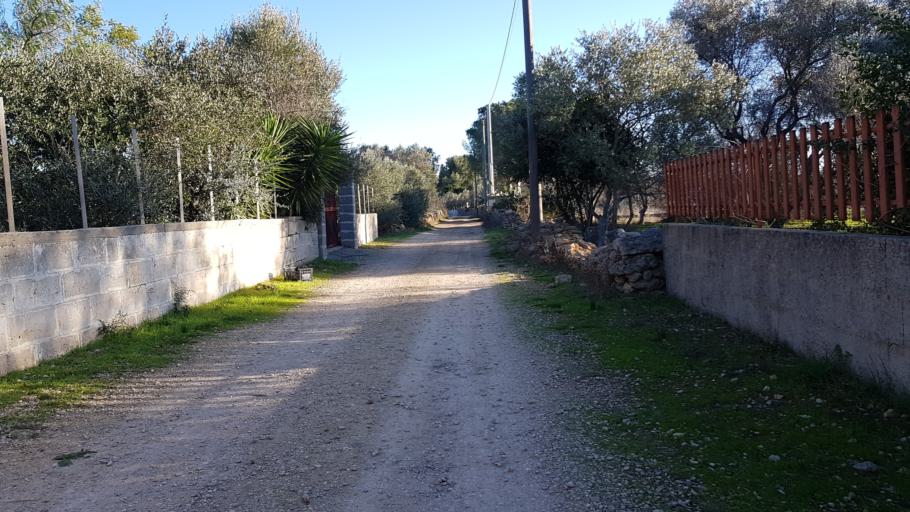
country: IT
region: Apulia
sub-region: Provincia di Lecce
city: Nardo
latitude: 40.1586
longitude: 17.9719
